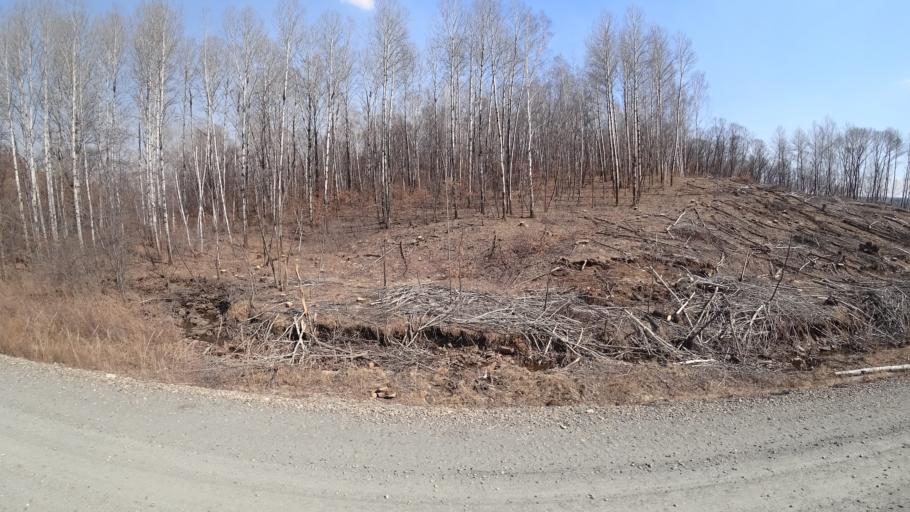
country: RU
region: Amur
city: Novobureyskiy
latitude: 49.7978
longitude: 129.9578
